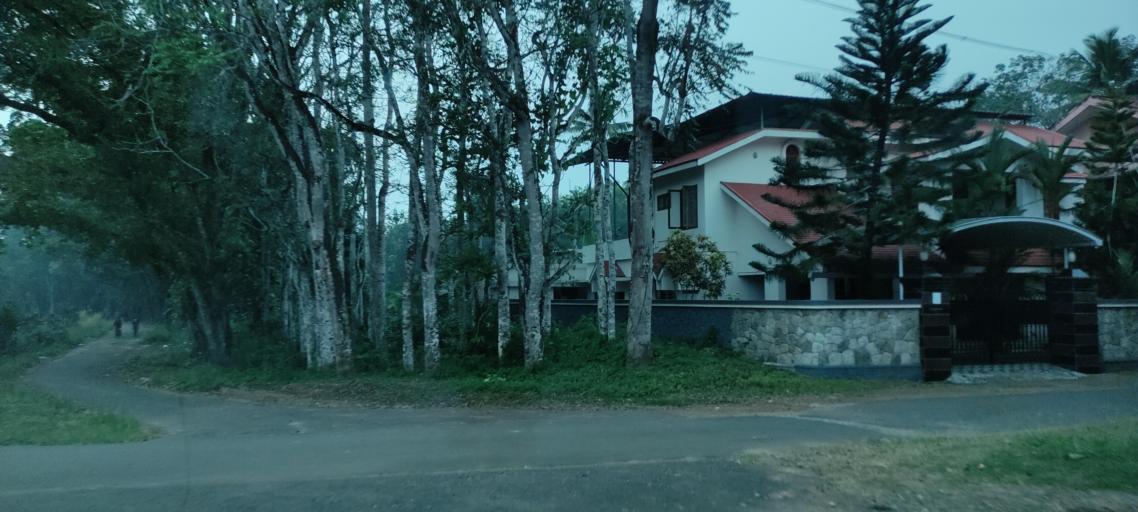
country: IN
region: Kerala
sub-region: Pattanamtitta
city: Adur
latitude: 9.1615
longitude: 76.7481
